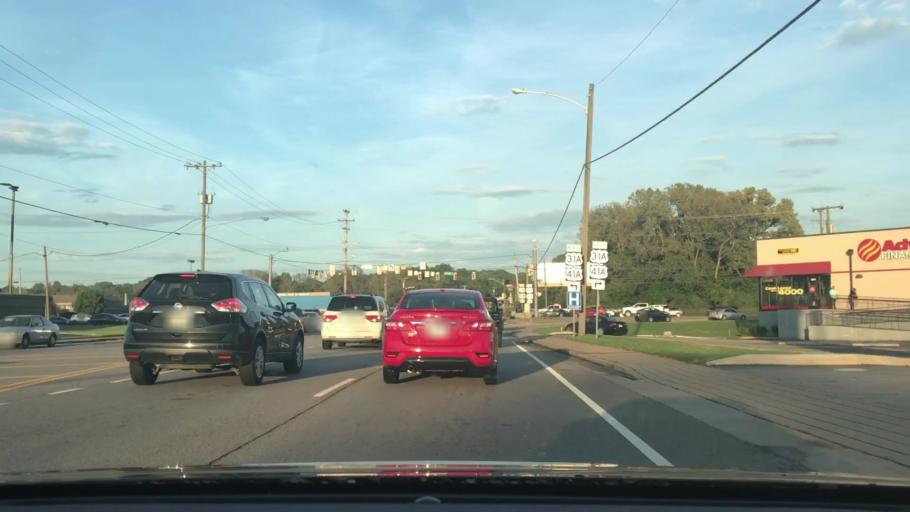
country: US
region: Tennessee
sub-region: Davidson County
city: Oak Hill
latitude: 36.0791
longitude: -86.7277
